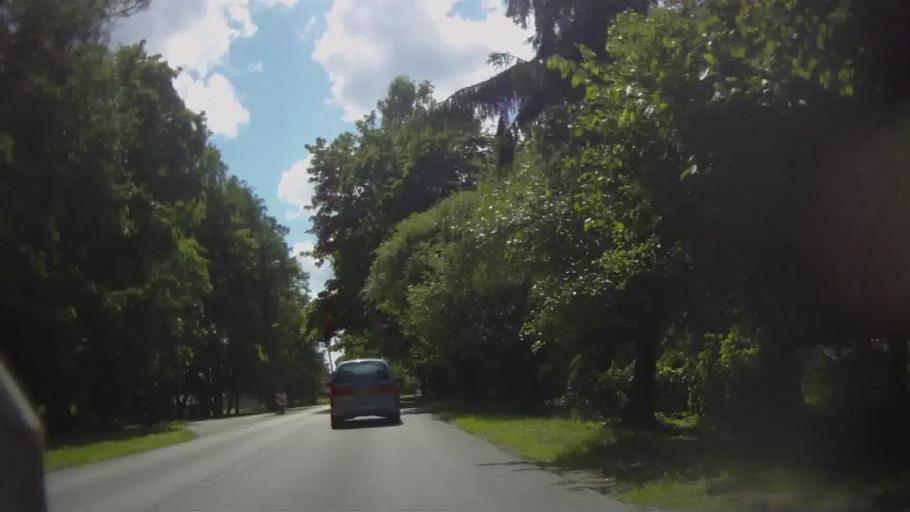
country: LV
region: Jurmala
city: Jurmala
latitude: 56.9525
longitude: 23.7687
